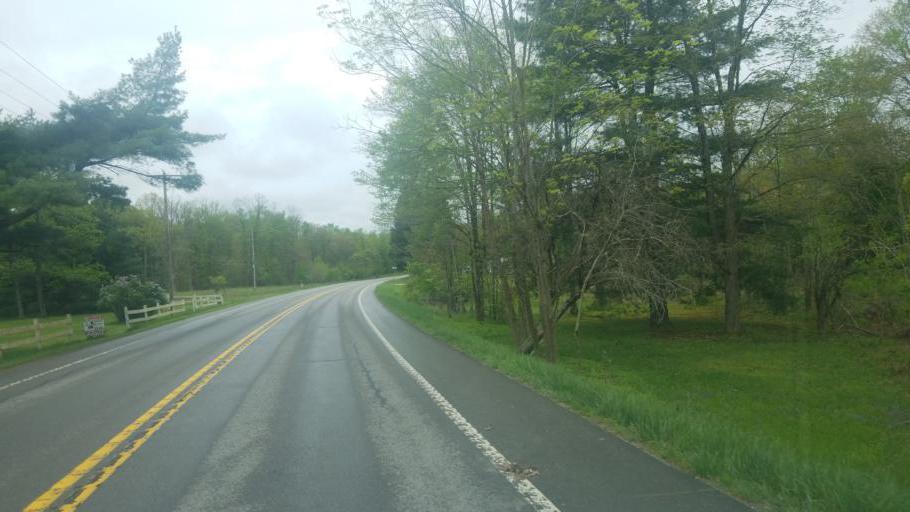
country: US
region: Pennsylvania
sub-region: Forest County
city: Marienville
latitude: 41.4325
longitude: -79.1879
